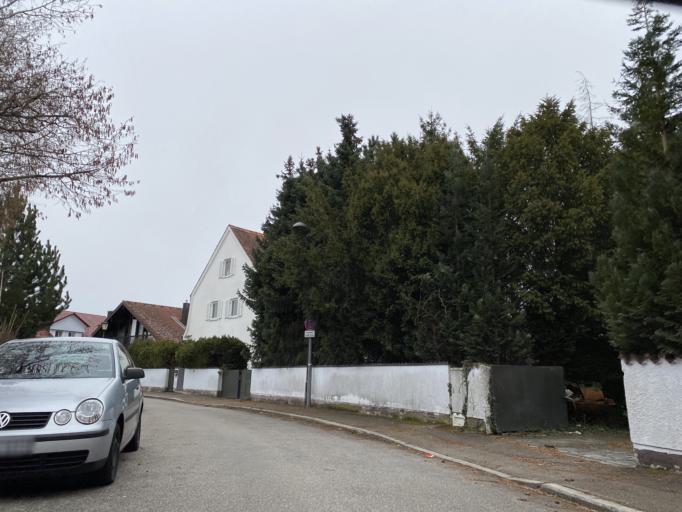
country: DE
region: Bavaria
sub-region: Upper Bavaria
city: Fuerstenfeldbruck
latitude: 48.1769
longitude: 11.2453
